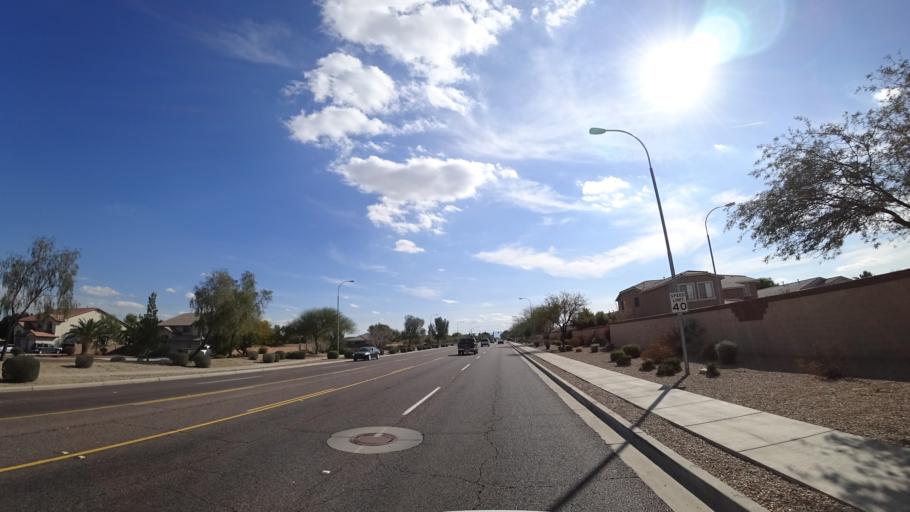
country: US
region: Arizona
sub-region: Maricopa County
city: Peoria
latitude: 33.6272
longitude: -112.2201
